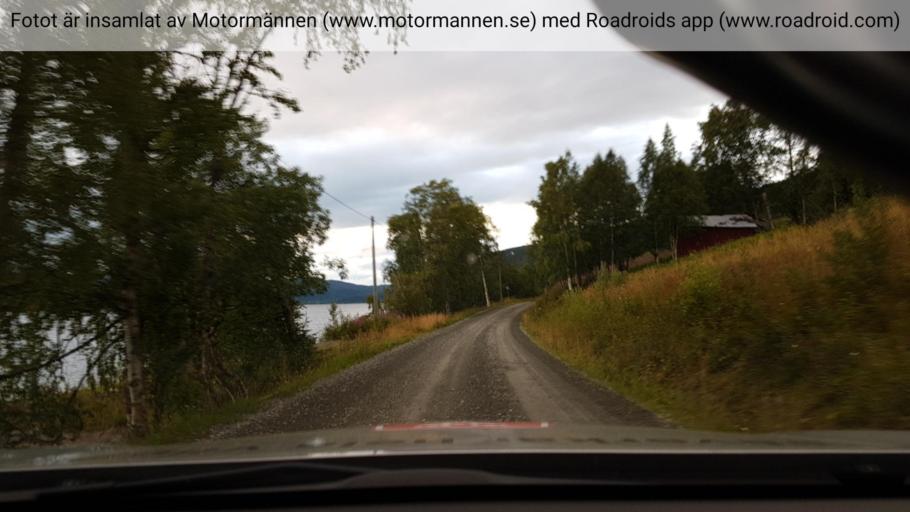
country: NO
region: Nordland
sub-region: Hattfjelldal
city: Hattfjelldal
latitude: 65.6219
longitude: 15.2383
